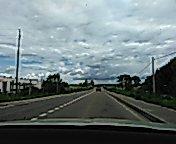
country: RU
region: Moskovskaya
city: Spas-Zaulok
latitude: 56.4760
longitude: 36.5858
